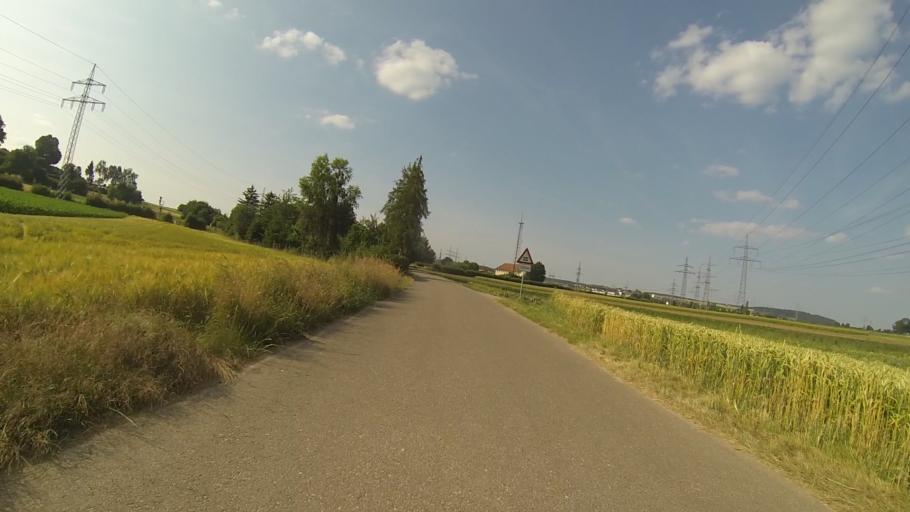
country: DE
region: Baden-Wuerttemberg
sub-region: Regierungsbezirk Stuttgart
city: Niederstotzingen
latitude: 48.5252
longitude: 10.2301
